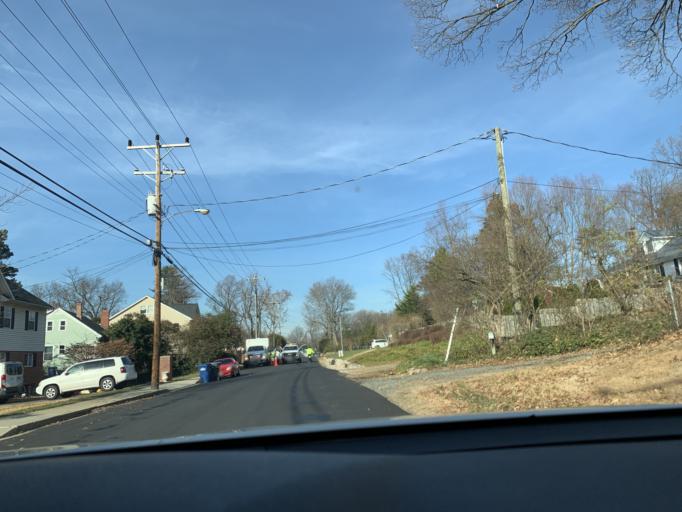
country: US
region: Virginia
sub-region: Fairfax County
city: Jefferson
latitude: 38.8549
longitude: -77.1850
